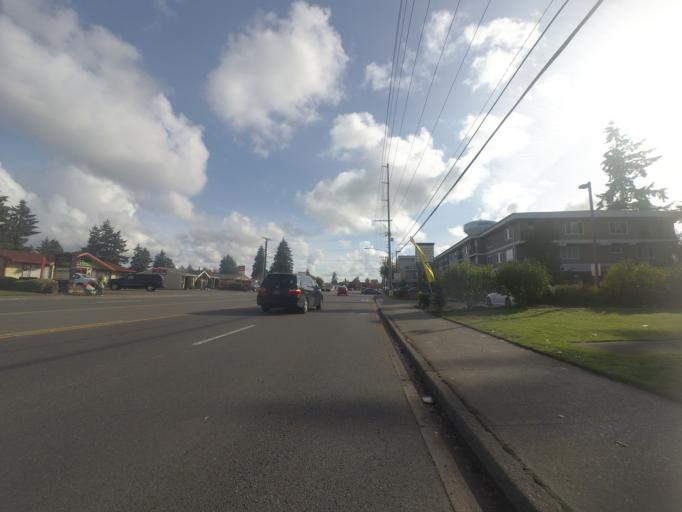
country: US
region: Washington
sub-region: Pierce County
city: Lakewood
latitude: 47.1645
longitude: -122.5075
